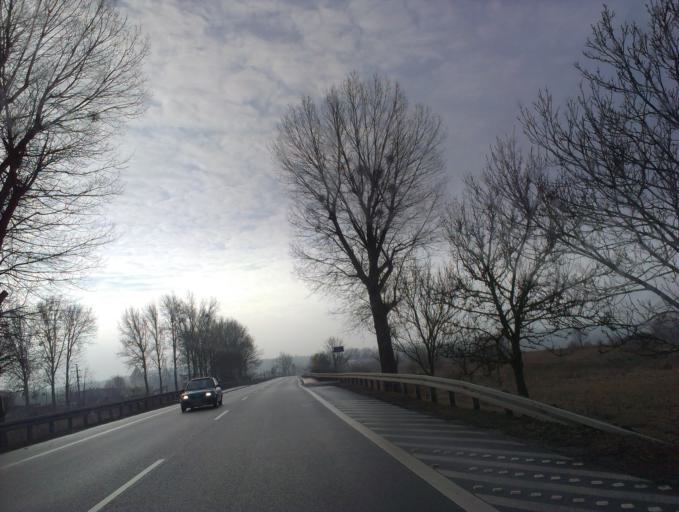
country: PL
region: Greater Poland Voivodeship
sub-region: Powiat pilski
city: Ujscie
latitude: 53.0670
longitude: 16.7306
